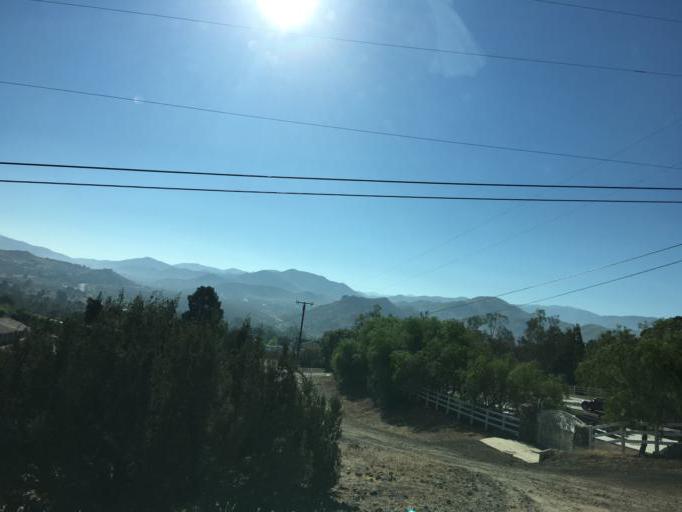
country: US
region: California
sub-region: Los Angeles County
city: Acton
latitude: 34.4680
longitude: -118.2068
